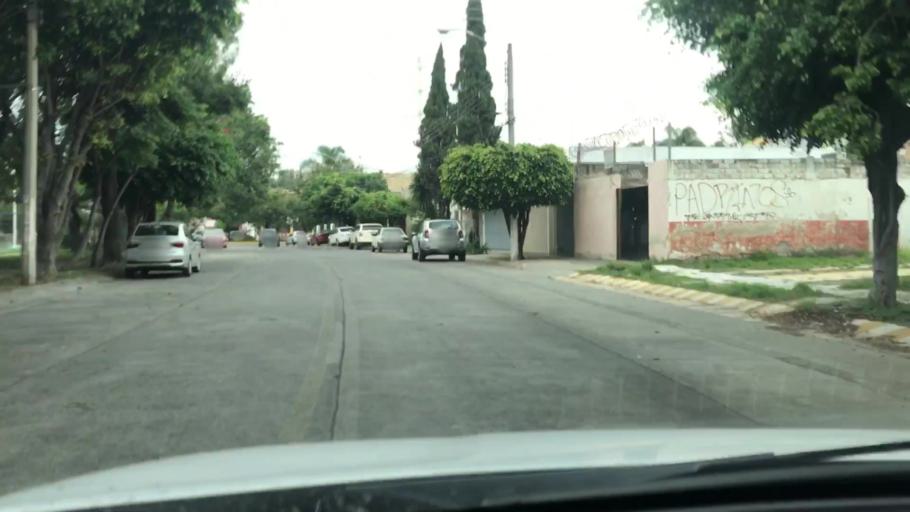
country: MX
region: Jalisco
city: Guadalajara
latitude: 20.6356
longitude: -103.4314
